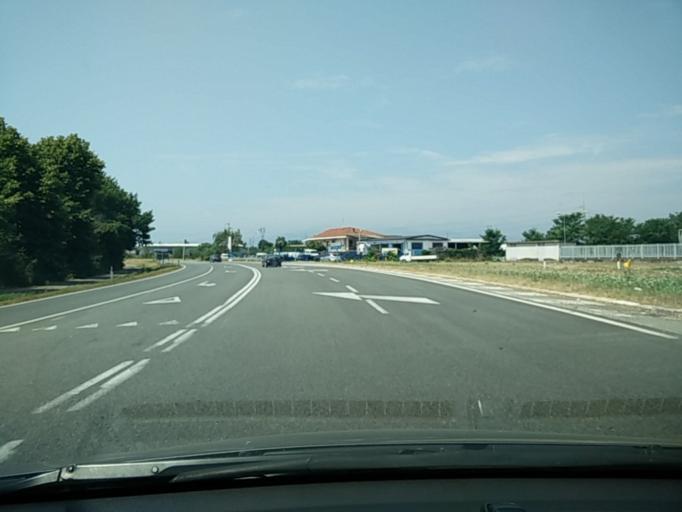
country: IT
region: Piedmont
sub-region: Provincia di Torino
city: Volpiano
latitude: 45.1899
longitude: 7.7495
